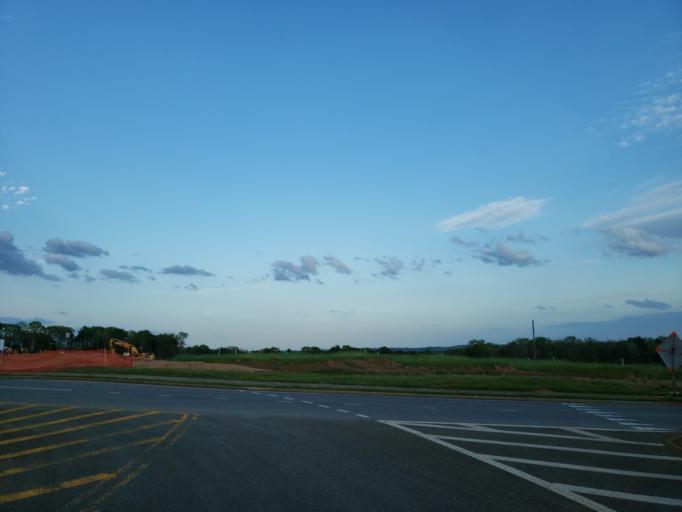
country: US
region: Georgia
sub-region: Cherokee County
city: Canton
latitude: 34.2732
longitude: -84.4707
